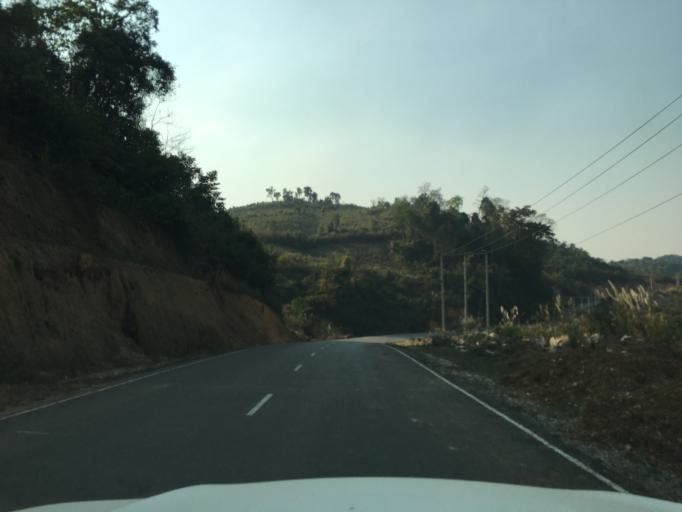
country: LA
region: Houaphan
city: Xam Nua
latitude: 20.5704
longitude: 104.0587
